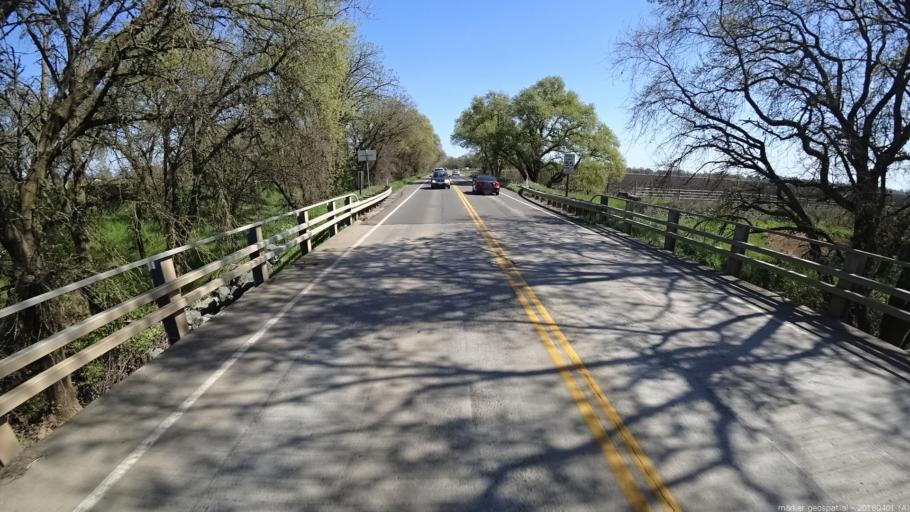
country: US
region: California
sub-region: Sacramento County
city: Wilton
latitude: 38.4206
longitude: -121.2855
